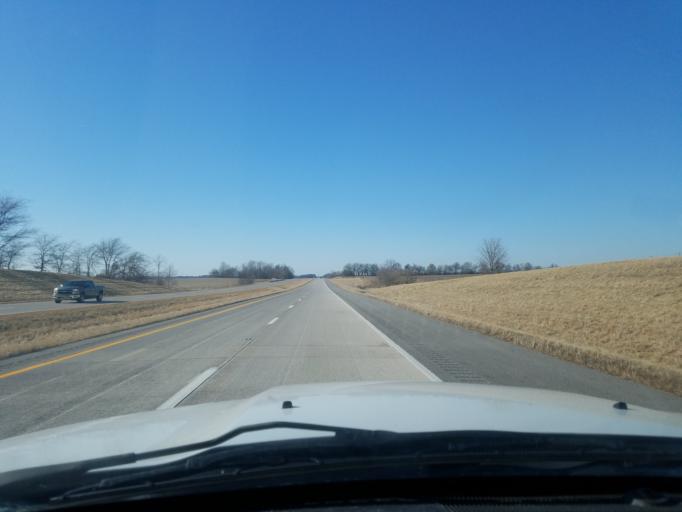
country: US
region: Kentucky
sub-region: Henderson County
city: Henderson
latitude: 37.7945
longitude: -87.4963
